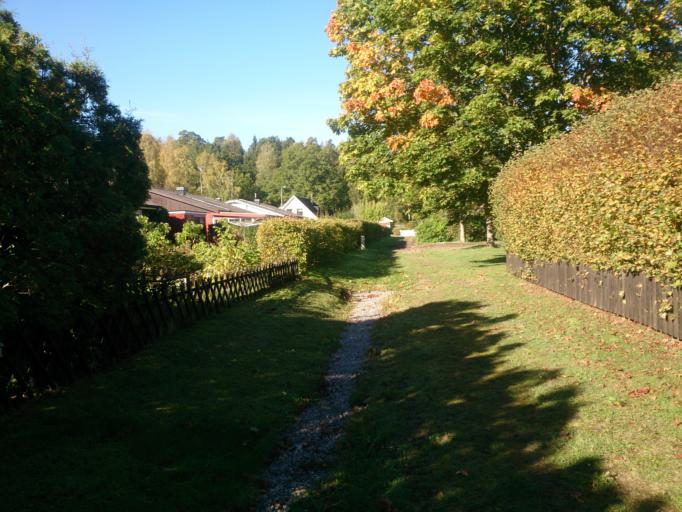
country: SE
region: OEstergoetland
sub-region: Linkopings Kommun
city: Sturefors
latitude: 58.3035
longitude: 15.8728
